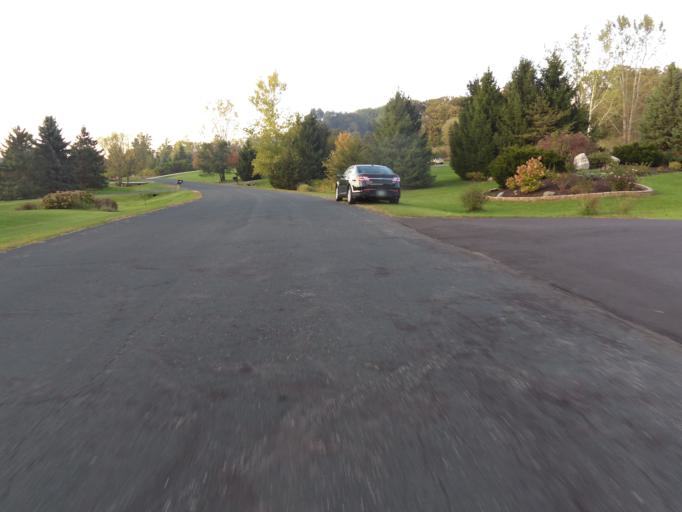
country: US
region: Minnesota
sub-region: Washington County
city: Lakeland
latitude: 44.9783
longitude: -92.8029
